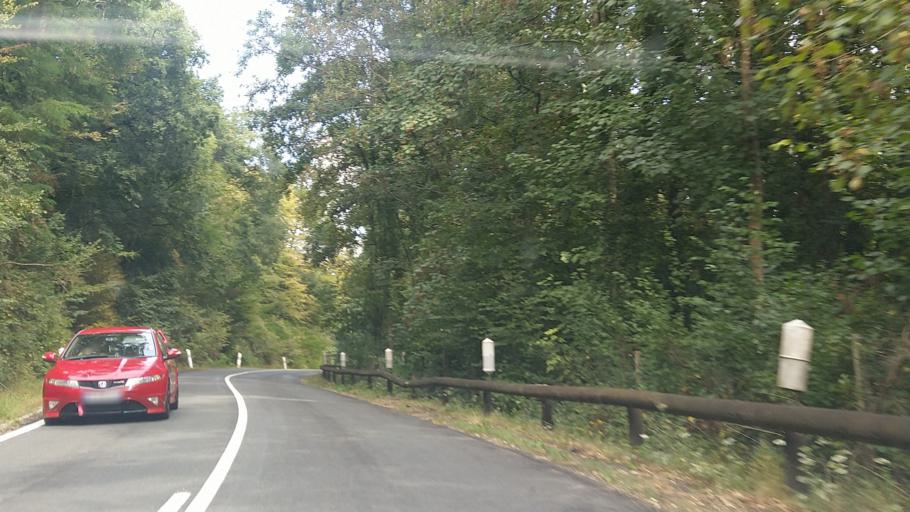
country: FR
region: Ile-de-France
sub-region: Departement des Yvelines
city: Saint-Arnoult-en-Yvelines
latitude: 48.5691
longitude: 1.9192
